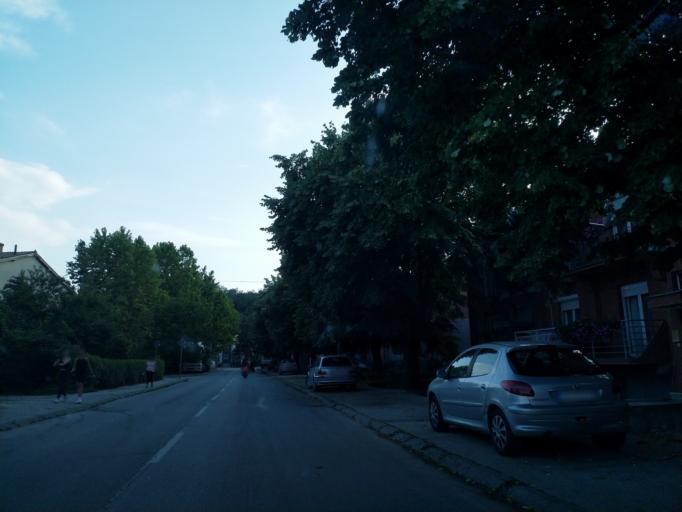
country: RS
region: Central Serbia
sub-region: Pomoravski Okrug
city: Jagodina
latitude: 43.9845
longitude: 21.2434
